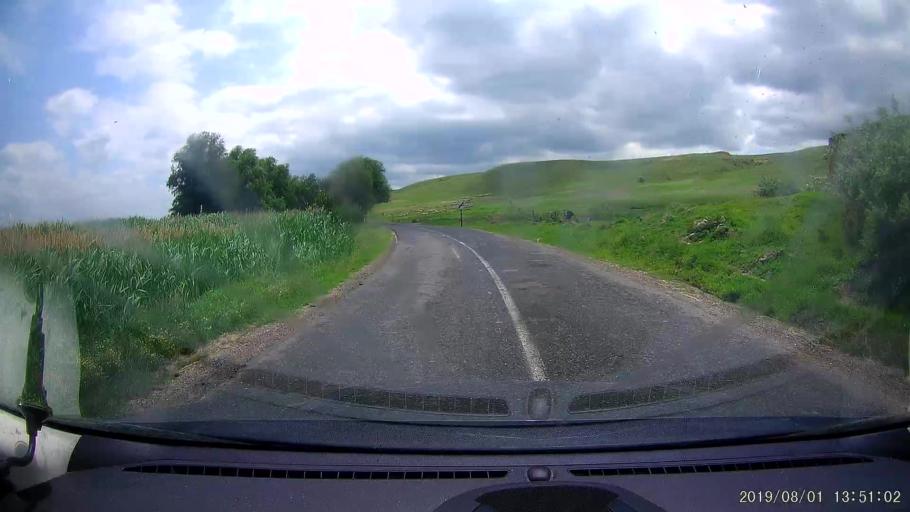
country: RO
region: Galati
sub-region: Comuna Vladesti
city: Vladesti
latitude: 45.8720
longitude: 28.0964
